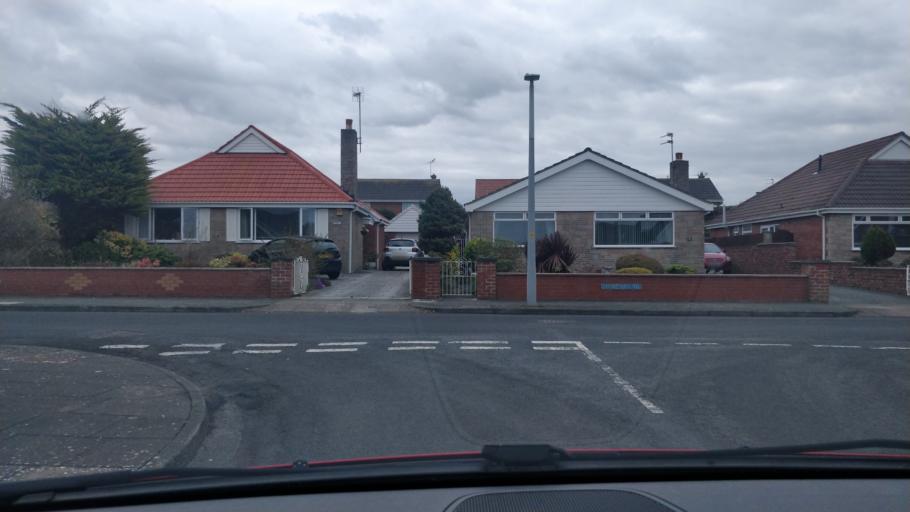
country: GB
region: England
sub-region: Sefton
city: Formby
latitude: 53.6064
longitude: -3.0496
